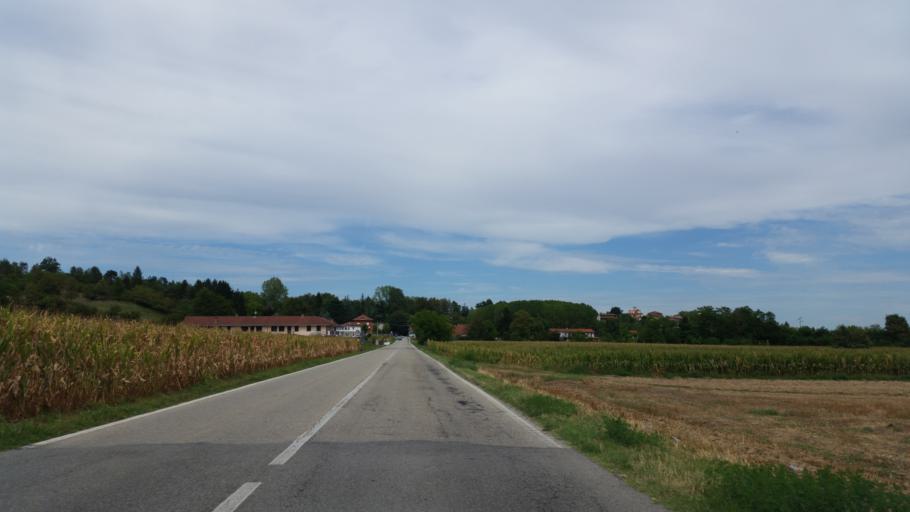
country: IT
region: Piedmont
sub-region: Provincia di Asti
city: Celle Enomondo
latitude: 44.8873
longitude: 8.1378
